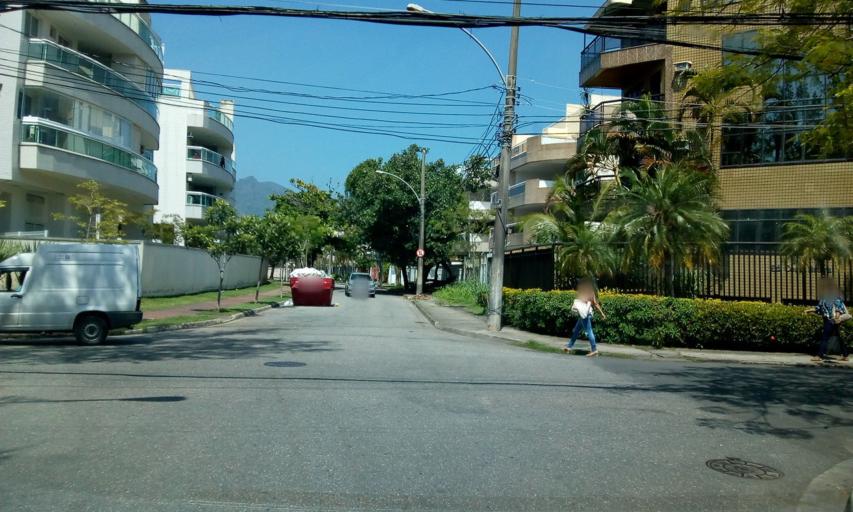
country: BR
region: Rio de Janeiro
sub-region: Nilopolis
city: Nilopolis
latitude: -23.0201
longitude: -43.4761
